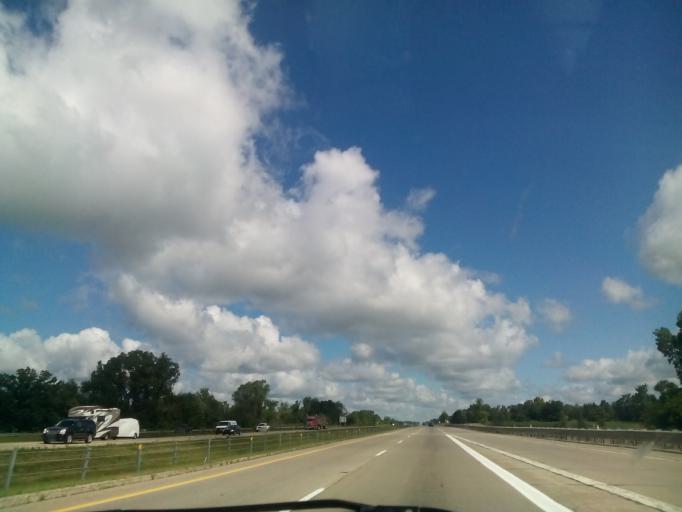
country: US
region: Michigan
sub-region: Genesee County
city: Fenton
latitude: 42.6793
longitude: -83.7598
